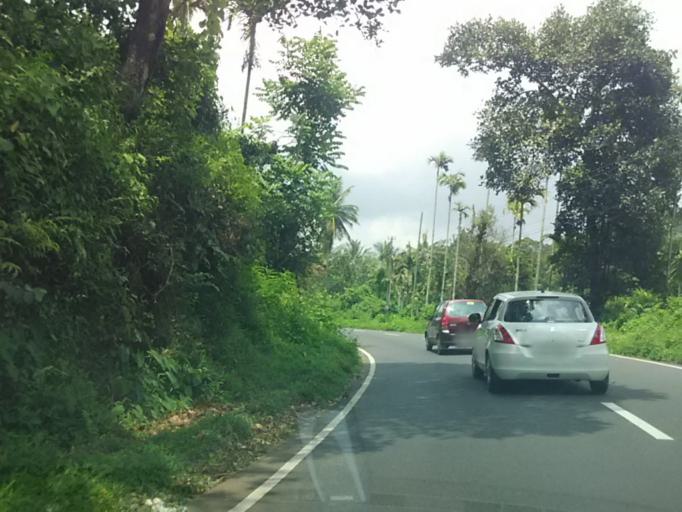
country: IN
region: Kerala
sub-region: Wayanad
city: Kalpetta
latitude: 11.5626
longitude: 76.0426
